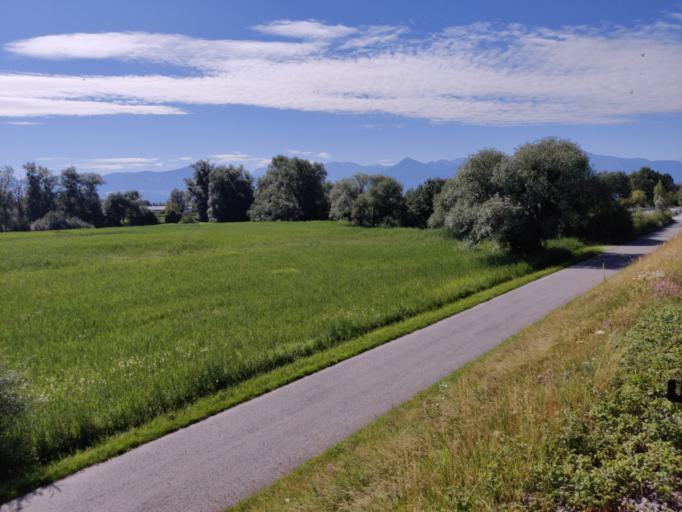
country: AT
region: Vorarlberg
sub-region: Politischer Bezirk Bregenz
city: Fussach
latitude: 47.4807
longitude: 9.6714
